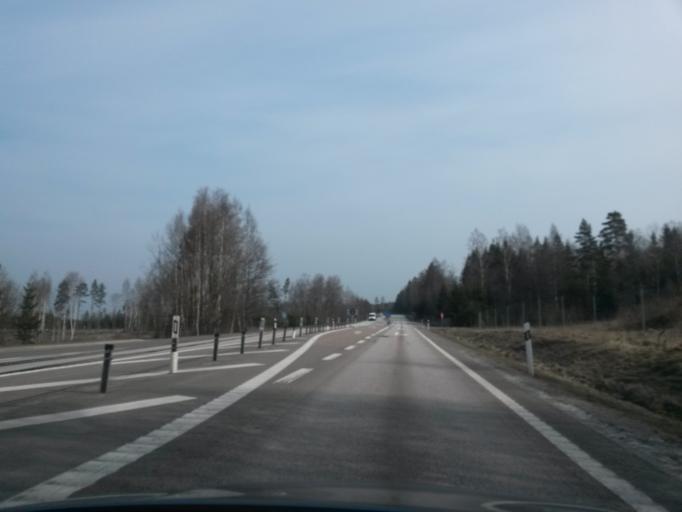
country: SE
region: Vaestra Goetaland
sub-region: Toreboda Kommun
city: Toereboda
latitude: 58.7766
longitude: 14.0023
